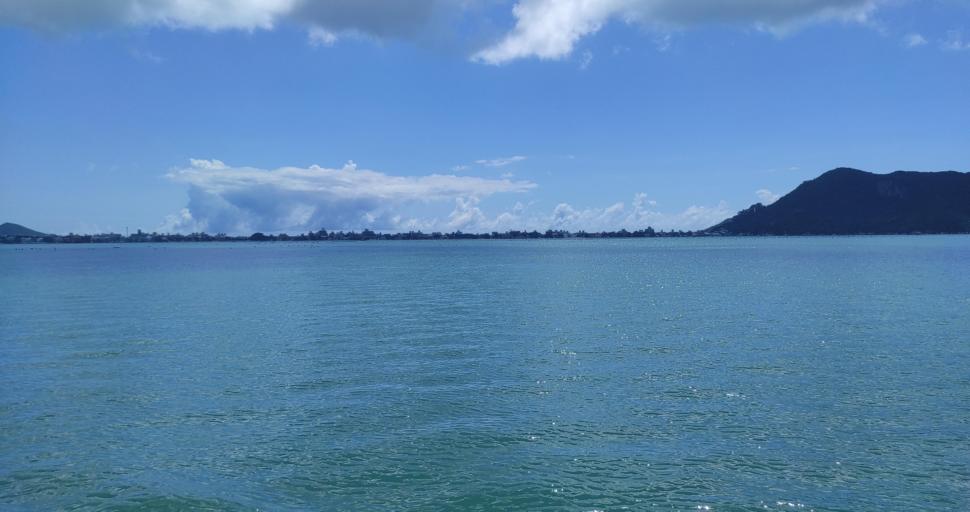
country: BR
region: Santa Catarina
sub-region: Porto Belo
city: Porto Belo
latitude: -27.2009
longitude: -48.5200
